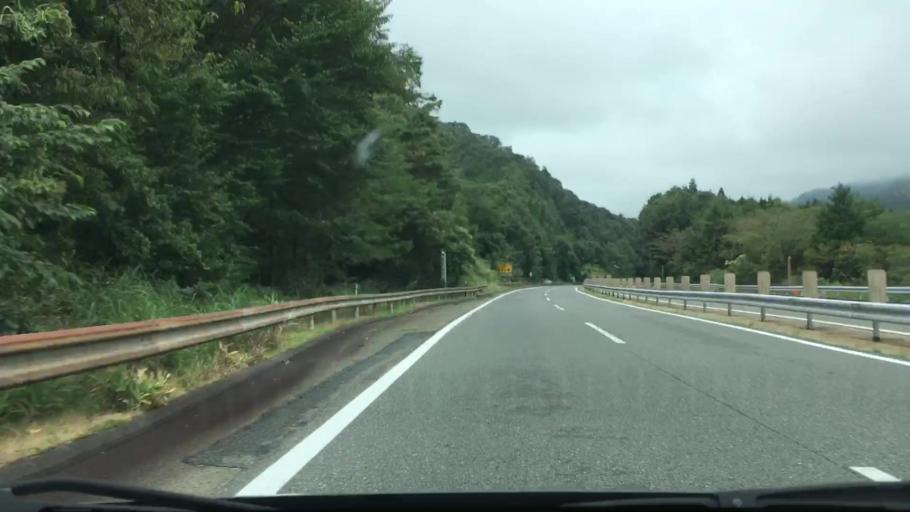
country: JP
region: Hiroshima
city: Shobara
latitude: 34.8695
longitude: 133.1160
